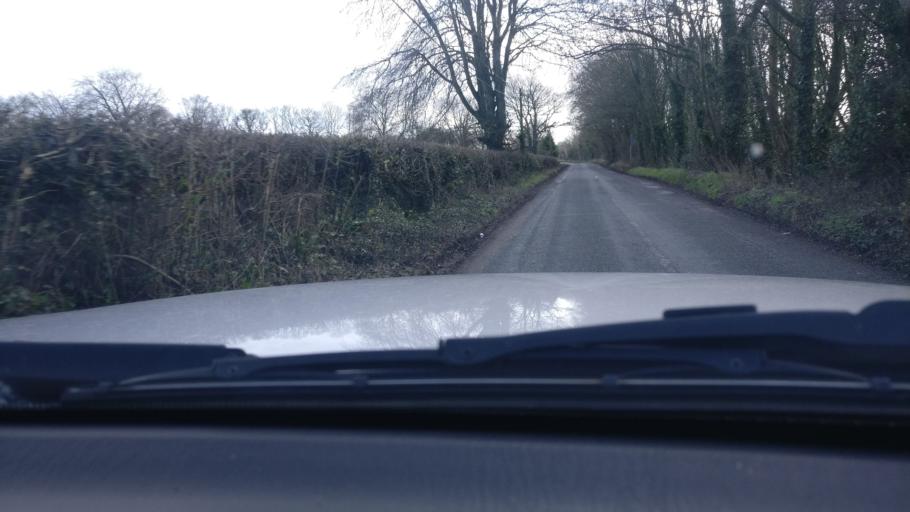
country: IE
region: Connaught
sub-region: County Galway
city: Ballinasloe
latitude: 53.2297
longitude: -8.2966
